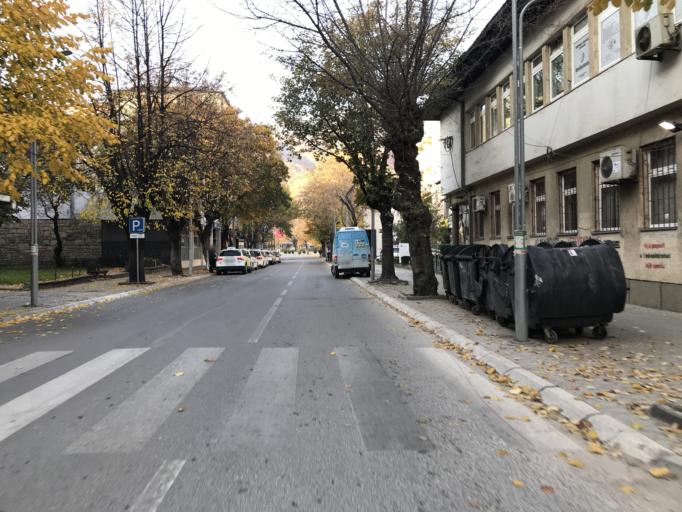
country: XK
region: Pec
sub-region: Komuna e Pejes
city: Peje
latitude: 42.6601
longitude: 20.2909
